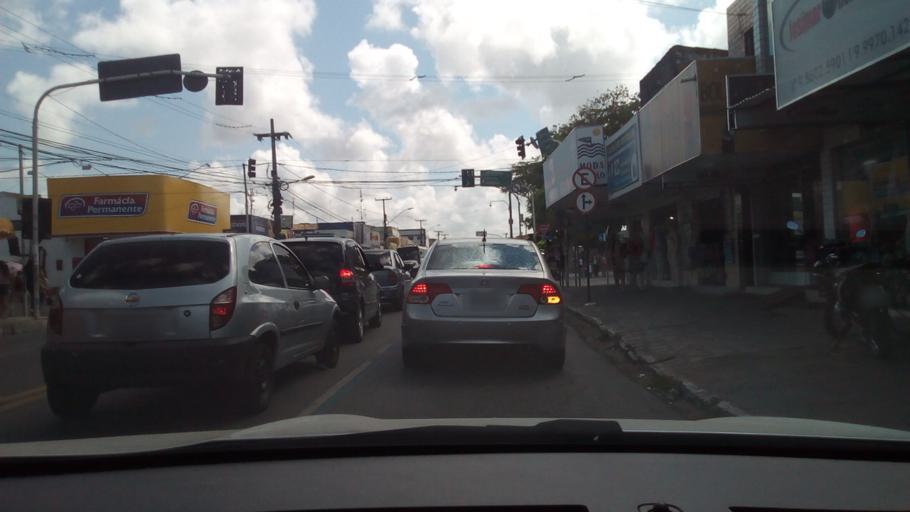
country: BR
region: Paraiba
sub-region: Joao Pessoa
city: Joao Pessoa
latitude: -7.1719
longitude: -34.8396
